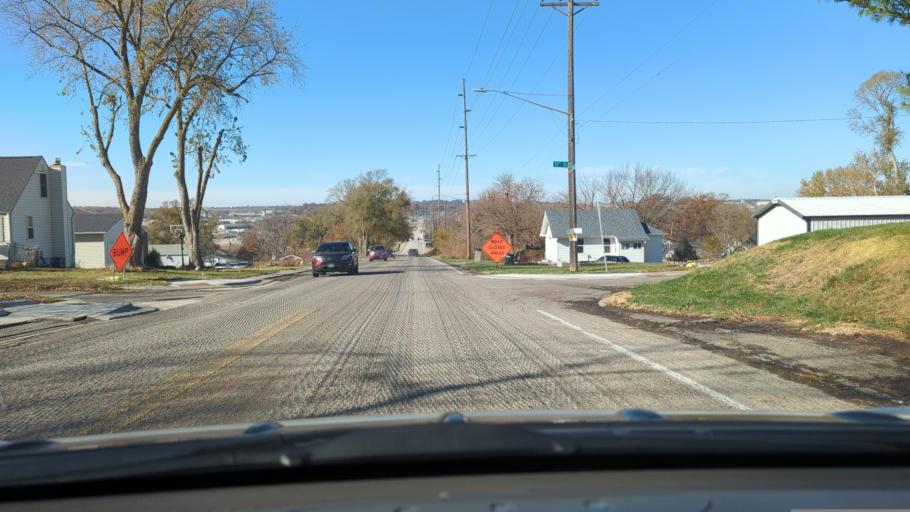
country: US
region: Nebraska
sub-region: Sarpy County
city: La Vista
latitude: 41.2053
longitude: -96.0010
